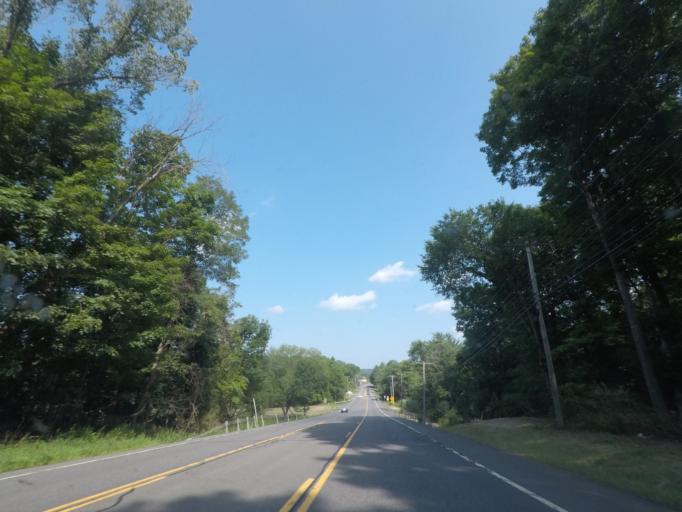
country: US
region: New York
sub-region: Rensselaer County
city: Nassau
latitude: 42.5199
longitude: -73.6308
